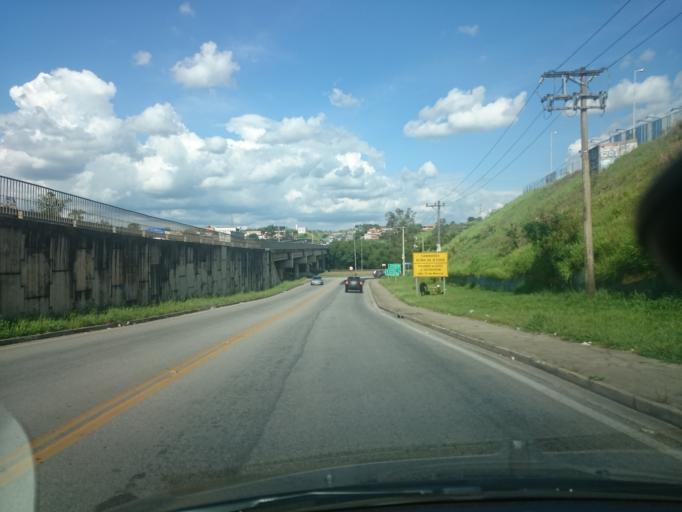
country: BR
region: Sao Paulo
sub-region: Votorantim
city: Votorantim
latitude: -23.5273
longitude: -47.4515
